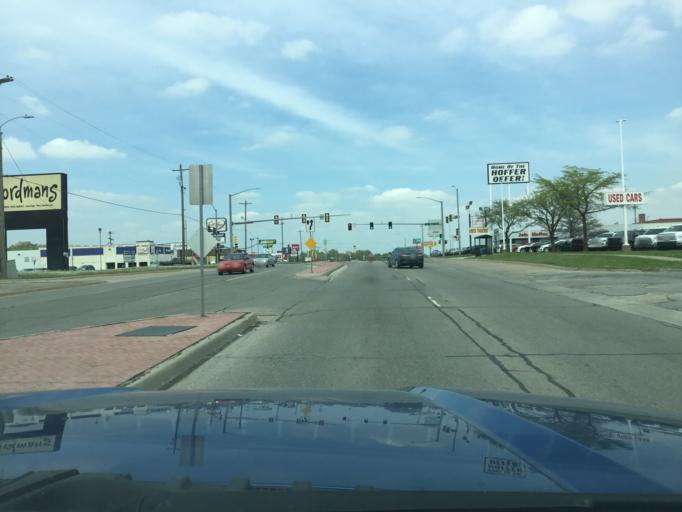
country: US
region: Kansas
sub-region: Shawnee County
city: Topeka
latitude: 39.0082
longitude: -95.6876
